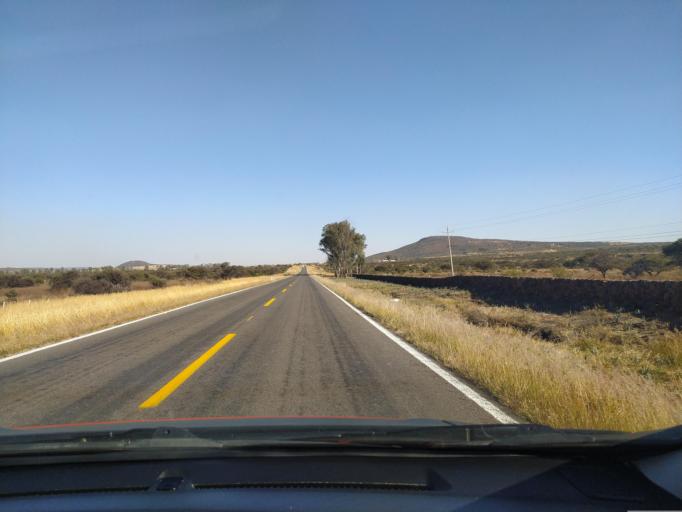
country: MX
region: Jalisco
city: San Miguel el Alto
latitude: 21.0165
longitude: -102.4825
